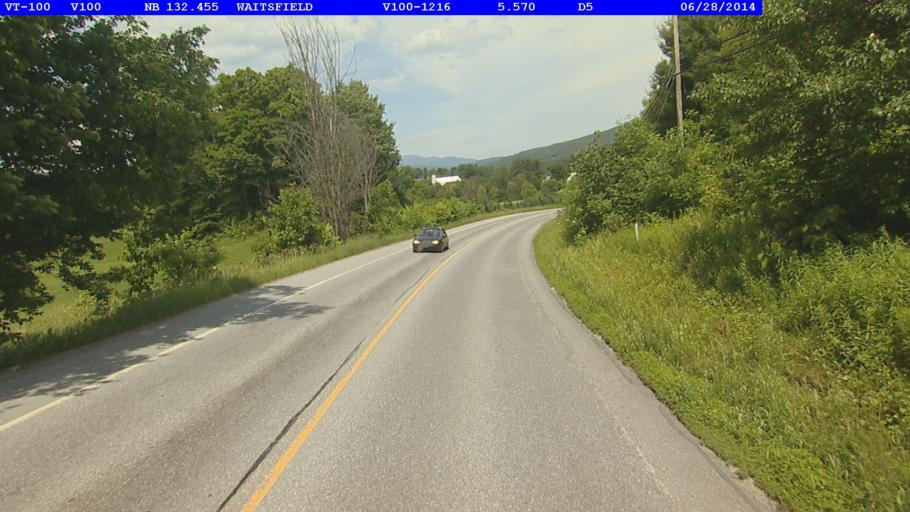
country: US
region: Vermont
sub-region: Washington County
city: Waterbury
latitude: 44.2102
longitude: -72.7987
